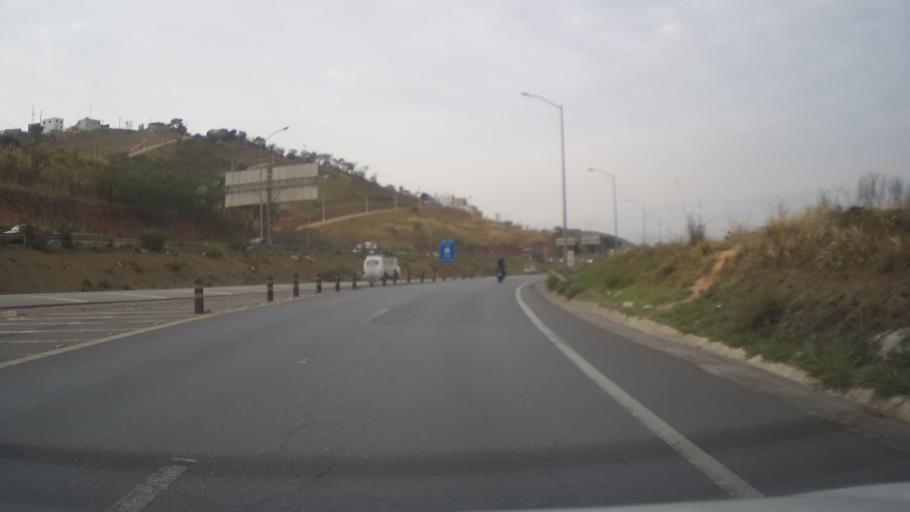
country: BR
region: Minas Gerais
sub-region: Vespasiano
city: Vespasiano
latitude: -19.7627
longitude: -43.9483
